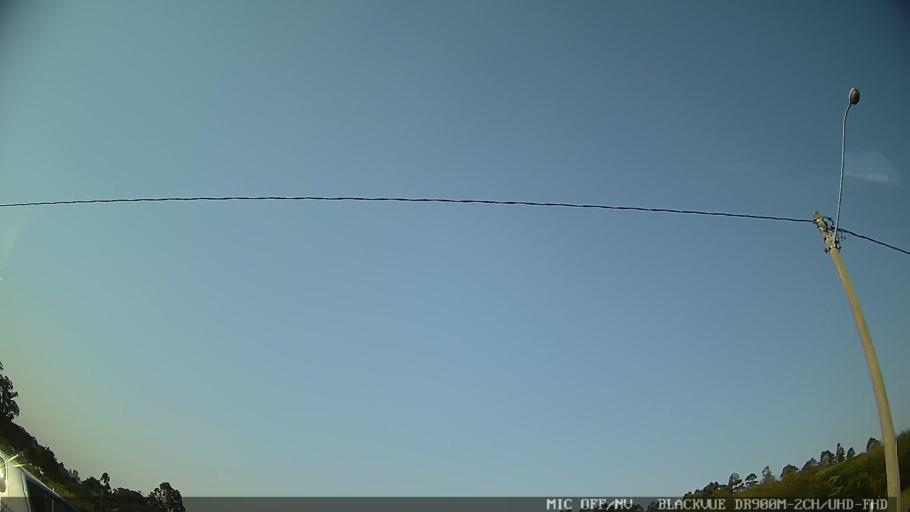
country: BR
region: Sao Paulo
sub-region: Itatiba
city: Itatiba
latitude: -23.0283
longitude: -46.8366
